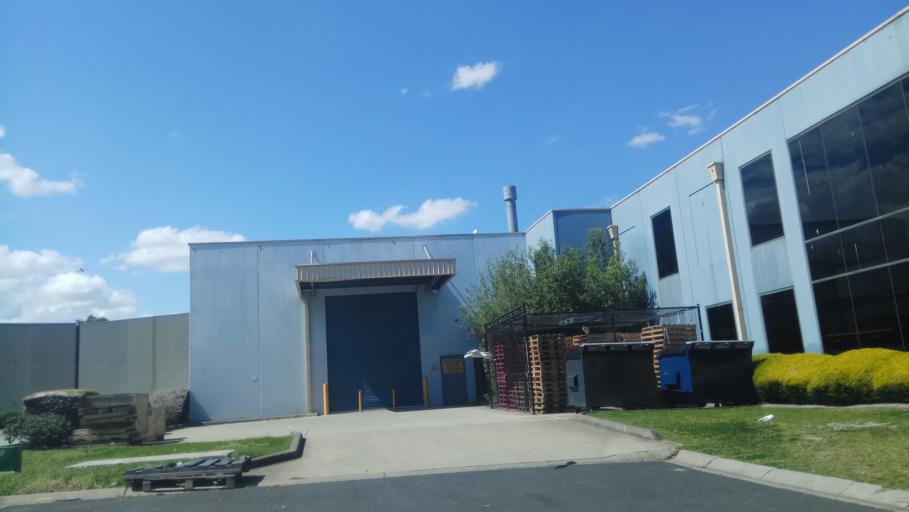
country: AU
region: Victoria
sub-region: Kingston
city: Dingley Village
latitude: -37.9935
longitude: 145.1170
